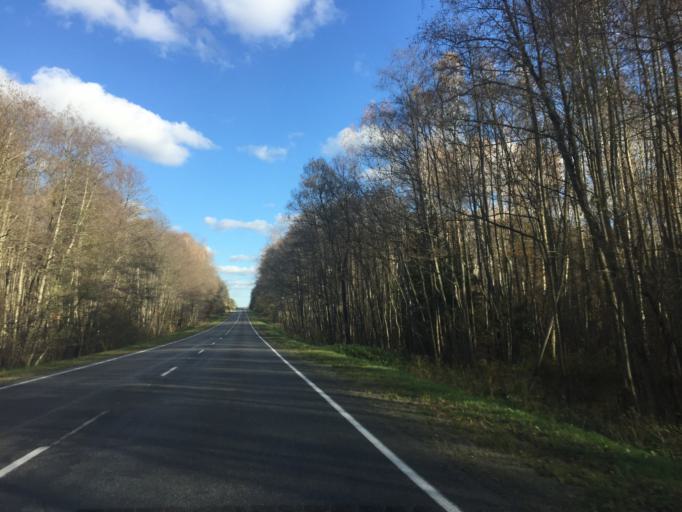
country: BY
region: Vitebsk
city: Pastavy
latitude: 55.0153
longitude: 26.8959
